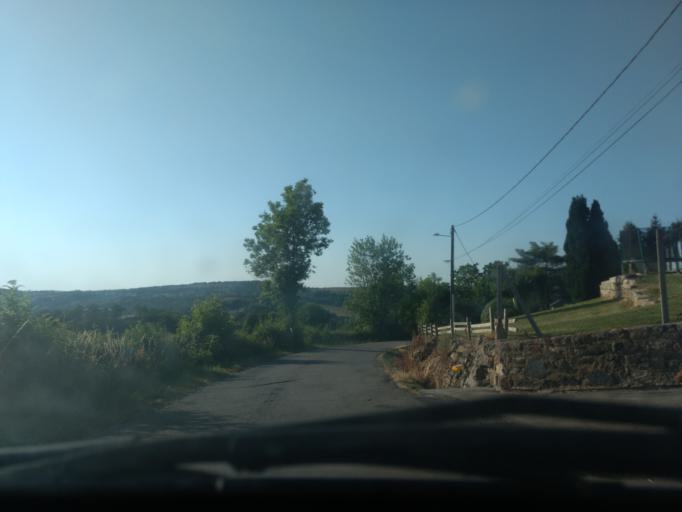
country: FR
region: Midi-Pyrenees
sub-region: Departement de l'Aveyron
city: La Loubiere
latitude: 44.3816
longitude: 2.7097
